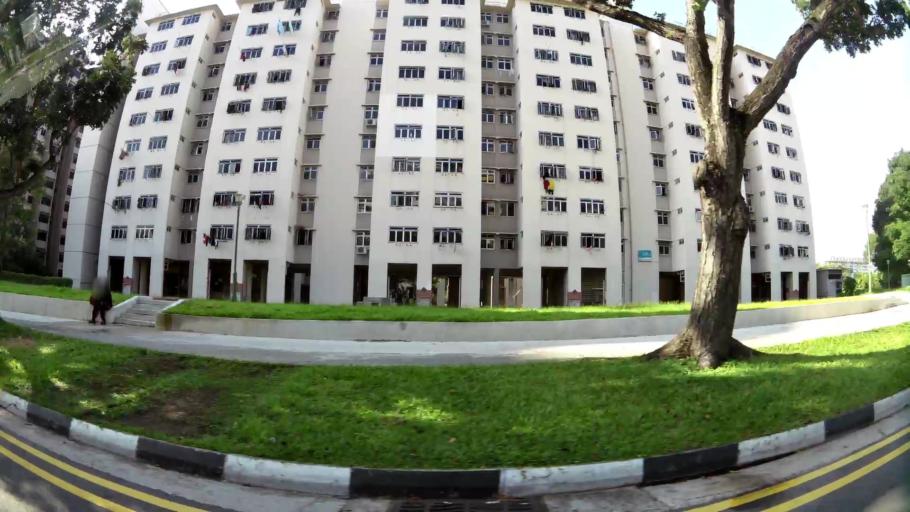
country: SG
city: Singapore
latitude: 1.3267
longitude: 103.9260
